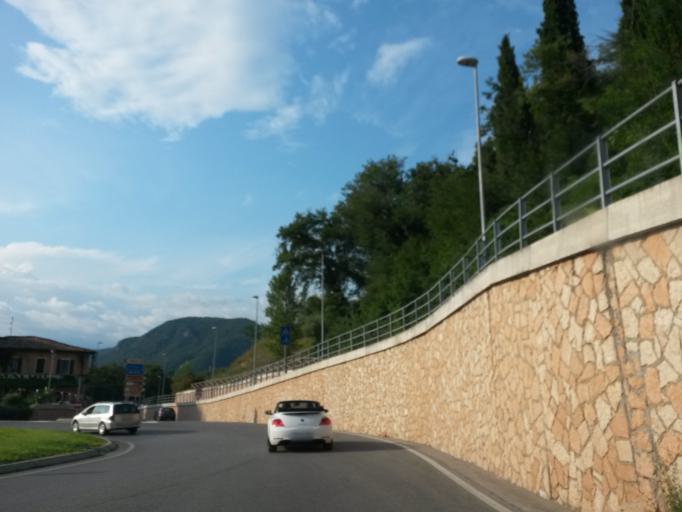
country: IT
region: Lombardy
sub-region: Provincia di Brescia
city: Cunettone-Villa
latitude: 45.5910
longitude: 10.5232
